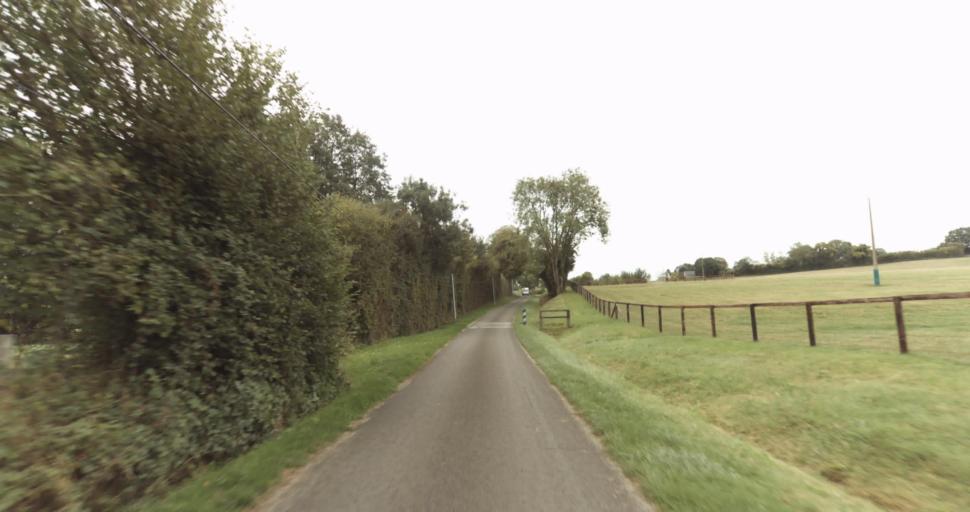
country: FR
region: Lower Normandy
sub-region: Departement de l'Orne
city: Gace
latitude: 48.7380
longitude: 0.2935
